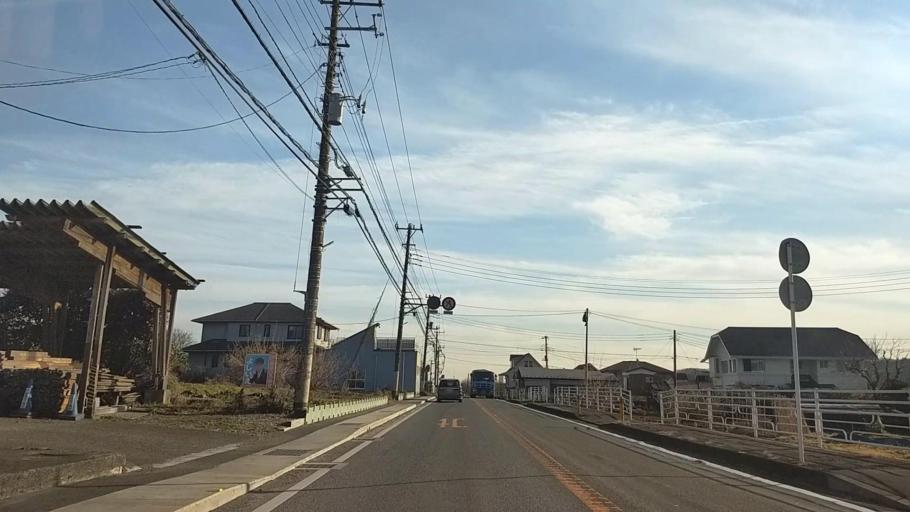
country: JP
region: Kanagawa
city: Zama
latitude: 35.5044
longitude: 139.3101
